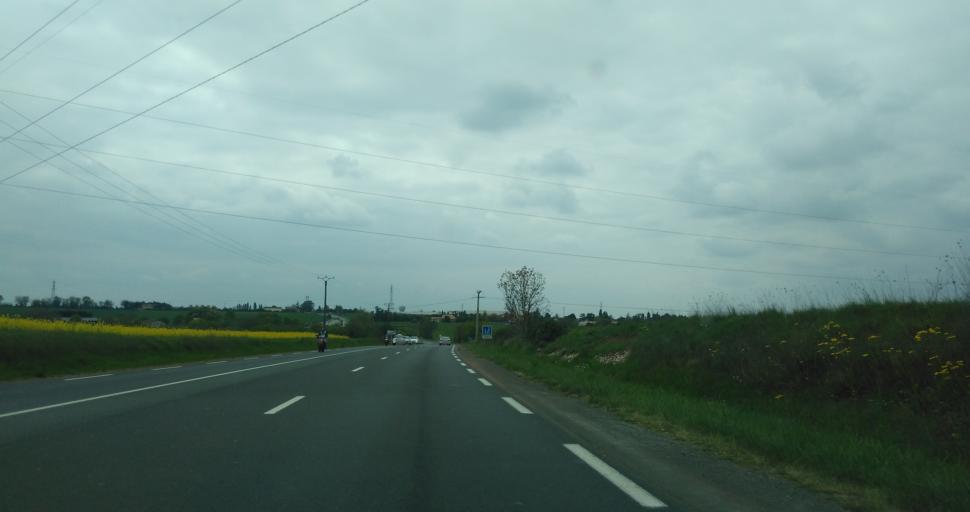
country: FR
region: Poitou-Charentes
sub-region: Departement des Deux-Sevres
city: Echire
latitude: 46.3594
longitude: -0.4340
